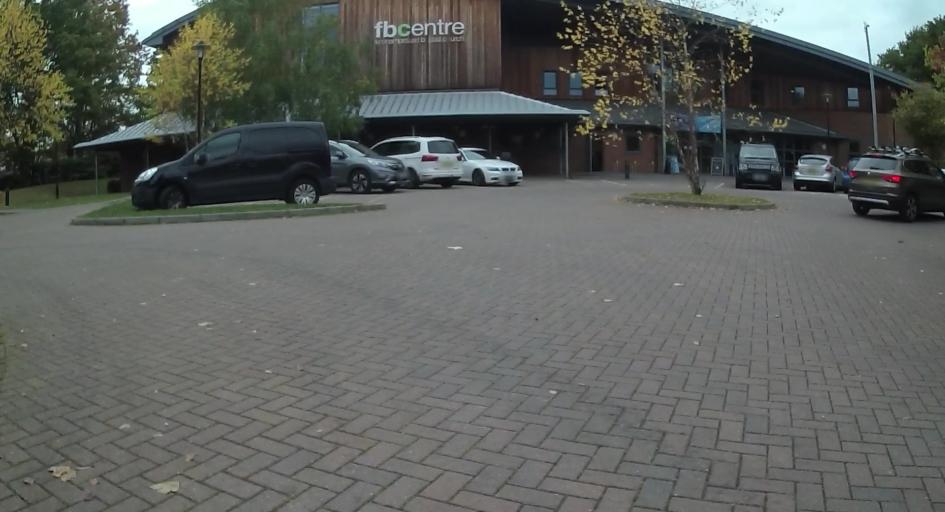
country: GB
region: England
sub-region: Wokingham
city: Finchampstead
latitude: 51.3792
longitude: -0.8610
